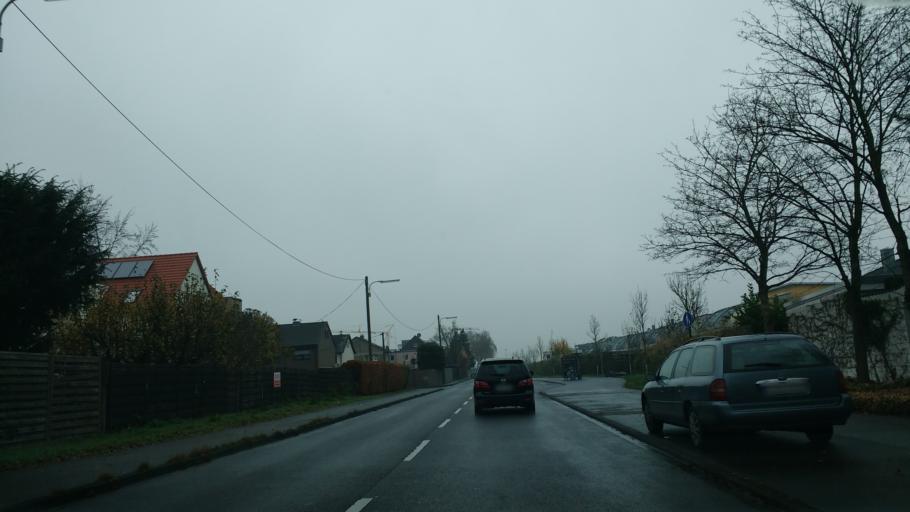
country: DE
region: North Rhine-Westphalia
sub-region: Regierungsbezirk Koln
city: Frechen
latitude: 50.9508
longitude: 6.8287
